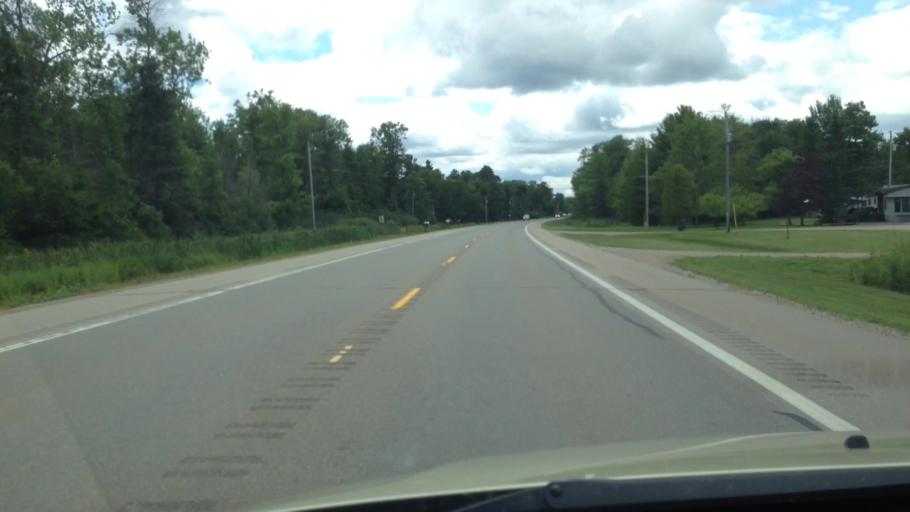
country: US
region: Michigan
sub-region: Menominee County
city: Menominee
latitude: 45.2215
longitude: -87.5158
